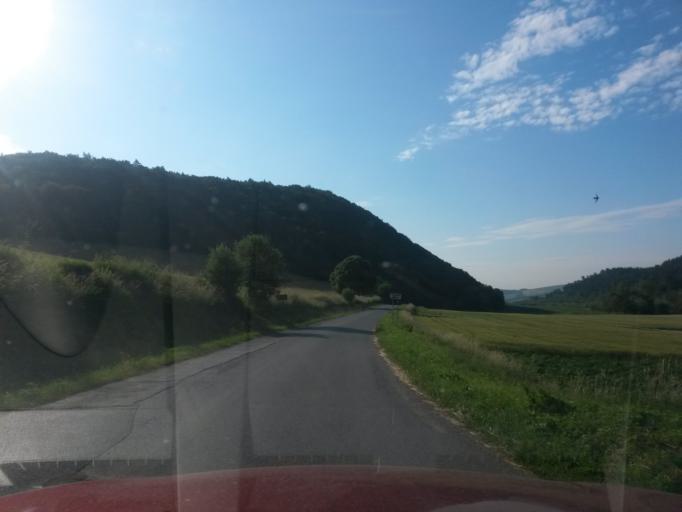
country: SK
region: Presovsky
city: Sabinov
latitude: 49.0856
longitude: 21.0281
